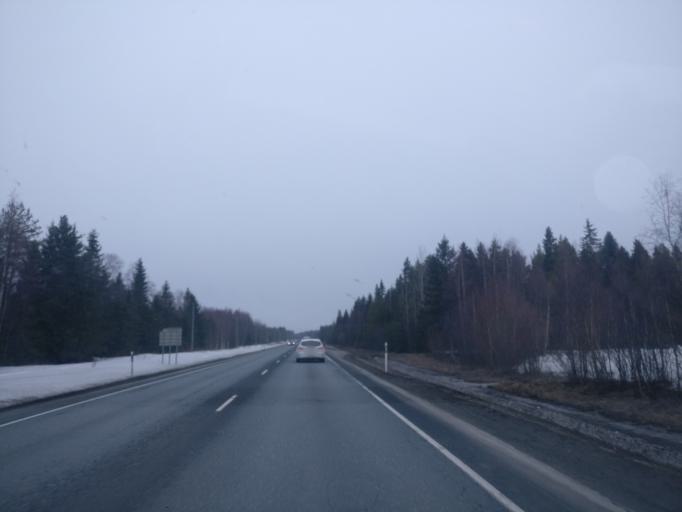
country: FI
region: Lapland
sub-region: Kemi-Tornio
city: Simo
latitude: 65.6708
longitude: 24.9206
